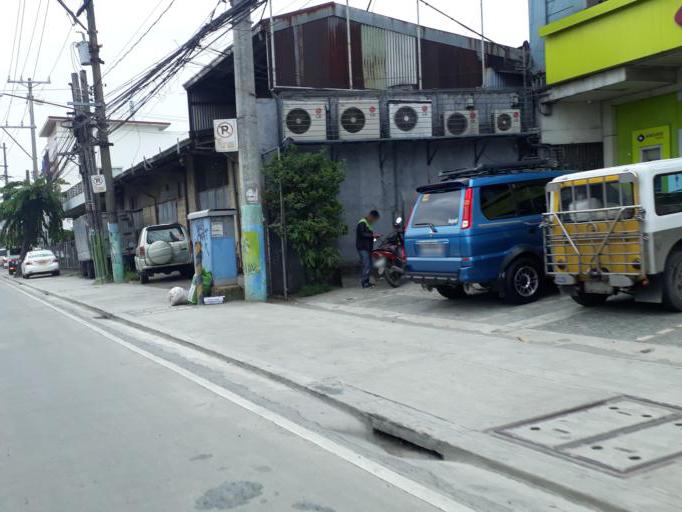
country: PH
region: Calabarzon
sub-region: Province of Rizal
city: Valenzuela
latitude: 14.7050
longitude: 120.9612
